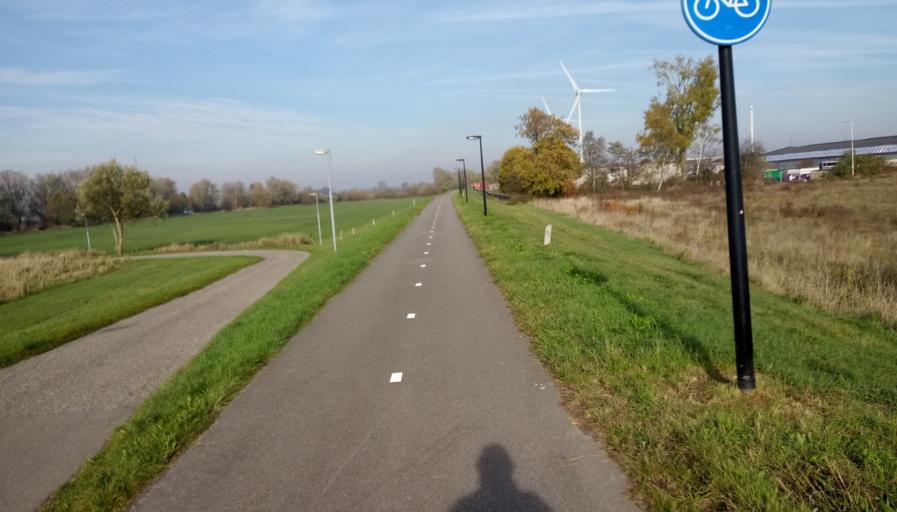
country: NL
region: Gelderland
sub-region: Gemeente Zutphen
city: Zutphen
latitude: 52.1524
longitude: 6.1884
